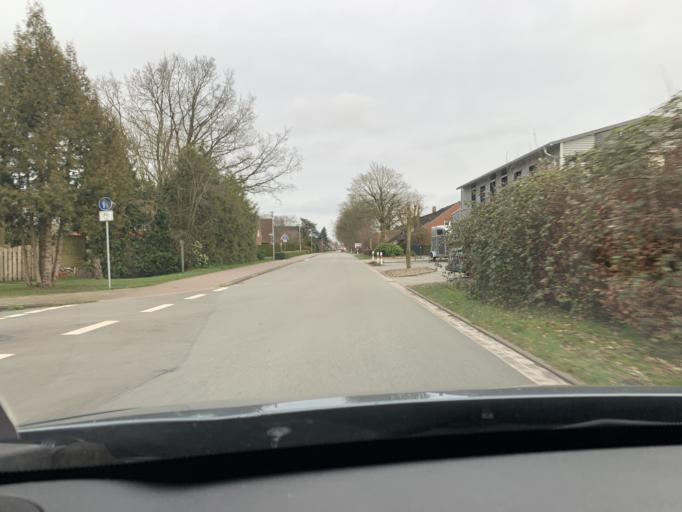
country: DE
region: Lower Saxony
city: Apen
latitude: 53.2263
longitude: 7.7488
